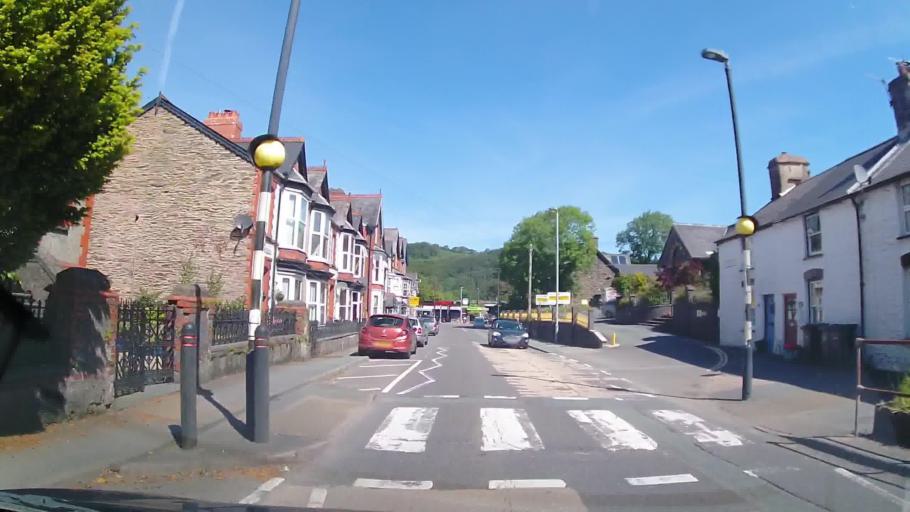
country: GB
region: Wales
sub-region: Sir Powys
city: Machynlleth
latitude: 52.5932
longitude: -3.8544
